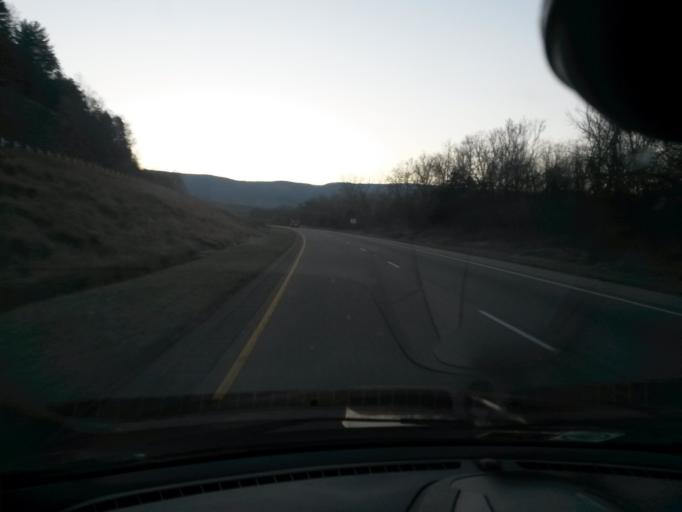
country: US
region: Virginia
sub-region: Alleghany County
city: Clifton Forge
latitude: 37.7983
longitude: -79.7307
